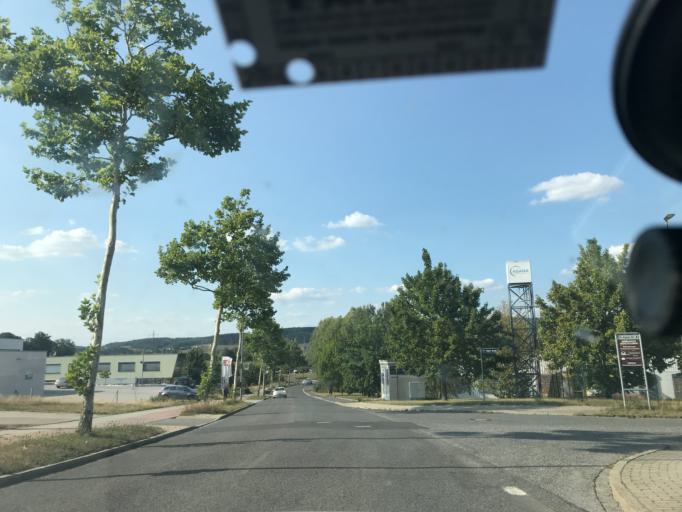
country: DE
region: Bavaria
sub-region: Upper Palatinate
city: Amberg
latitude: 49.4466
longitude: 11.8261
